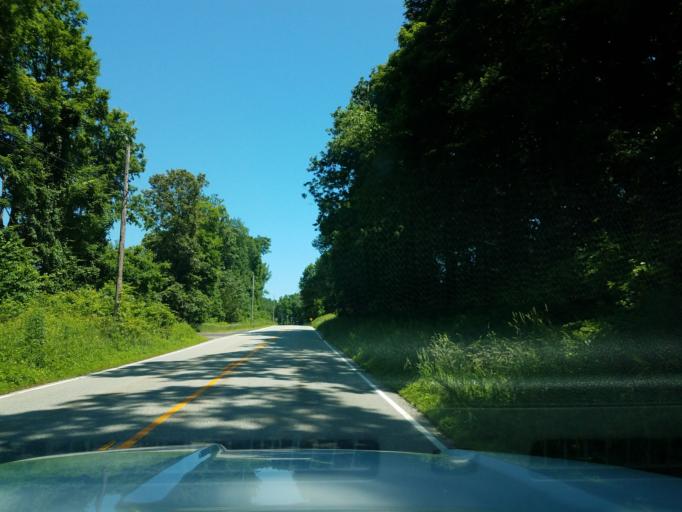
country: US
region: Connecticut
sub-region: New London County
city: Baltic
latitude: 41.6538
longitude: -72.0926
